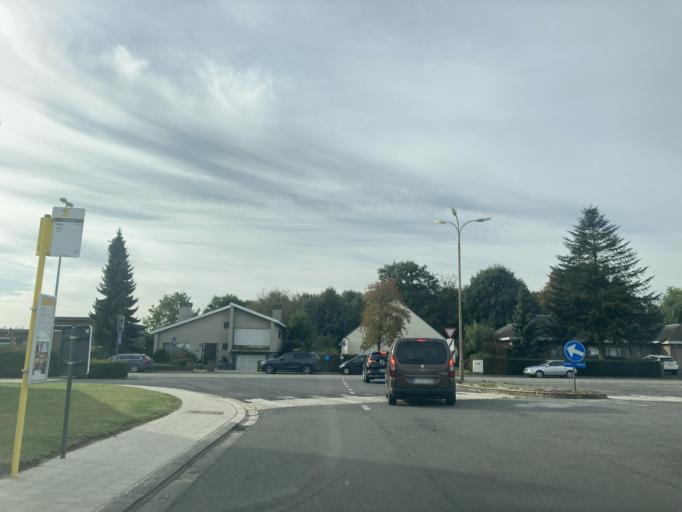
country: BE
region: Flanders
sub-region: Provincie West-Vlaanderen
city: Wervik
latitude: 50.7823
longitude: 3.0286
